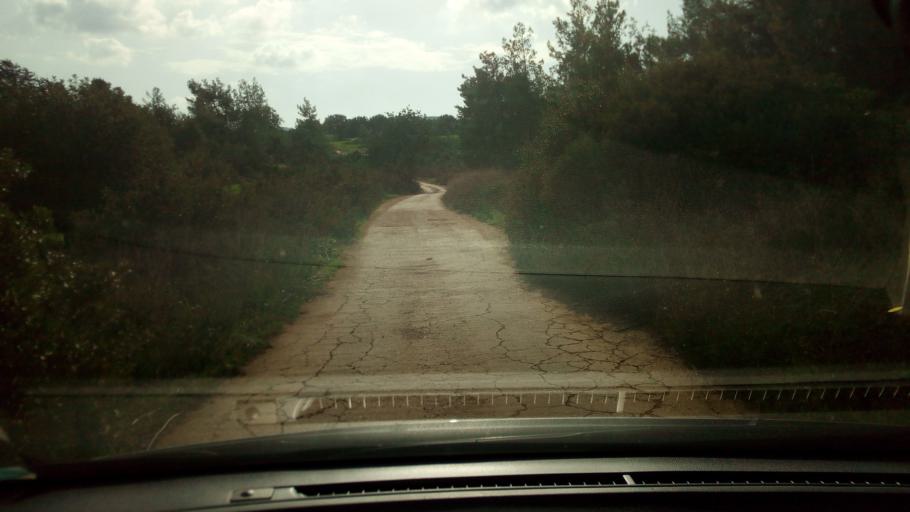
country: CY
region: Pafos
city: Polis
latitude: 35.0224
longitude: 32.3552
